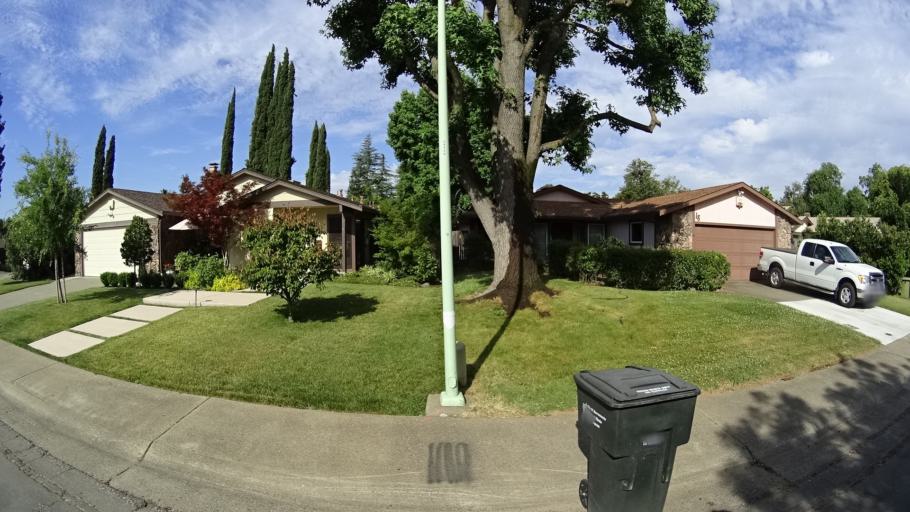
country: US
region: California
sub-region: Sacramento County
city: Rosemont
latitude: 38.5607
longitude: -121.3865
